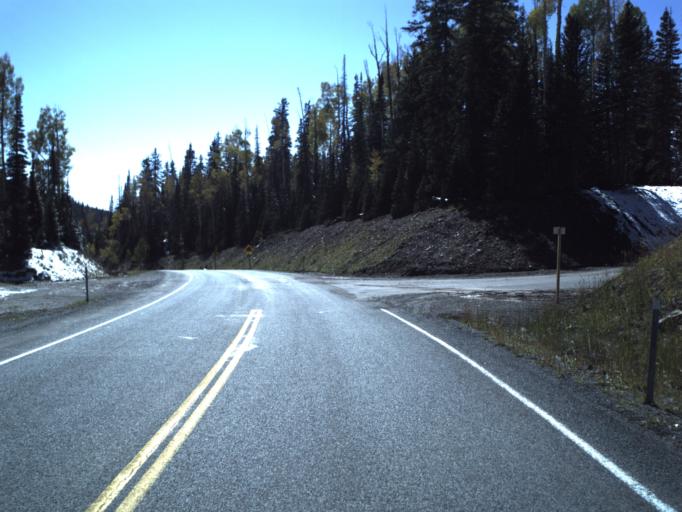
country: US
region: Utah
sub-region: Piute County
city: Junction
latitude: 38.3260
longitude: -112.3740
